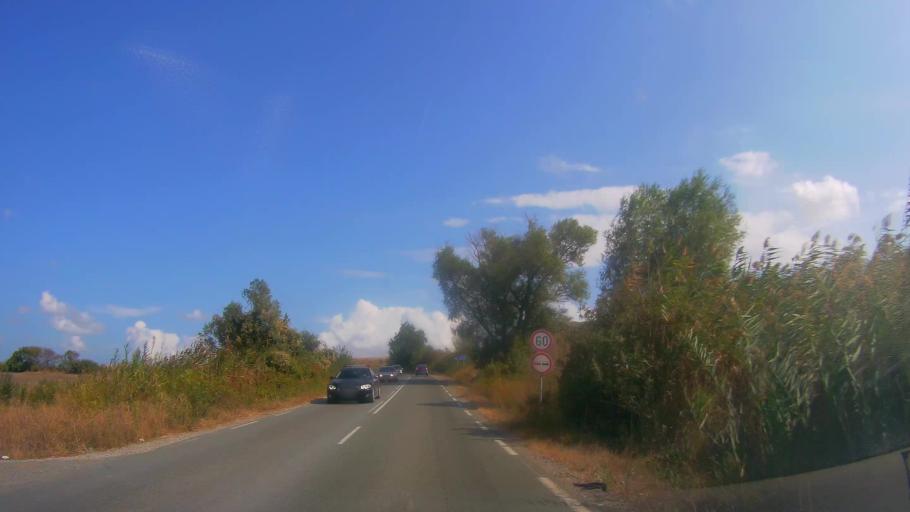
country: BG
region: Burgas
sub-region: Obshtina Burgas
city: Burgas
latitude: 42.4742
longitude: 27.3609
